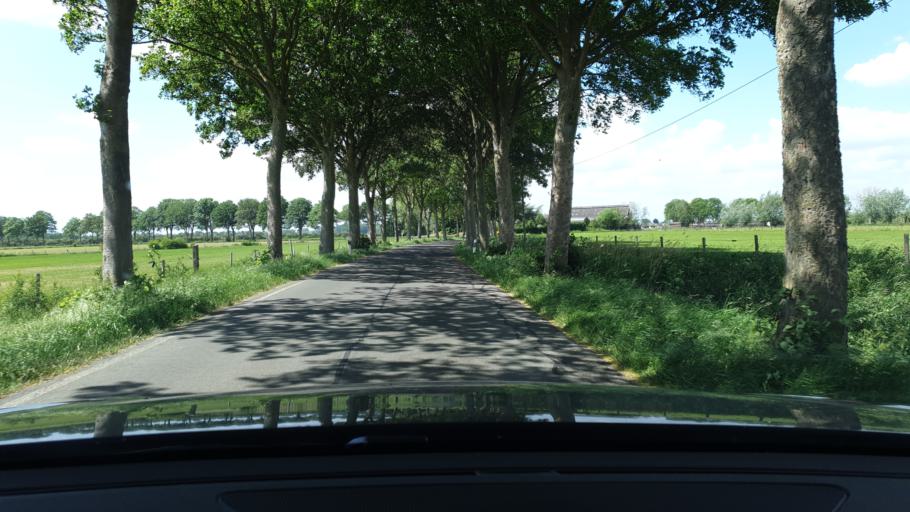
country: DE
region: North Rhine-Westphalia
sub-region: Regierungsbezirk Dusseldorf
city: Kranenburg
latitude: 51.8266
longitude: 6.0033
